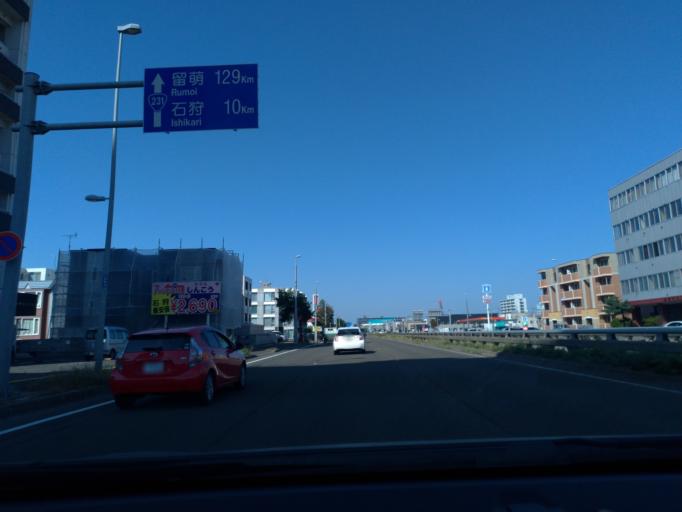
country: JP
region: Hokkaido
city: Sapporo
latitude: 43.1026
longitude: 141.3447
